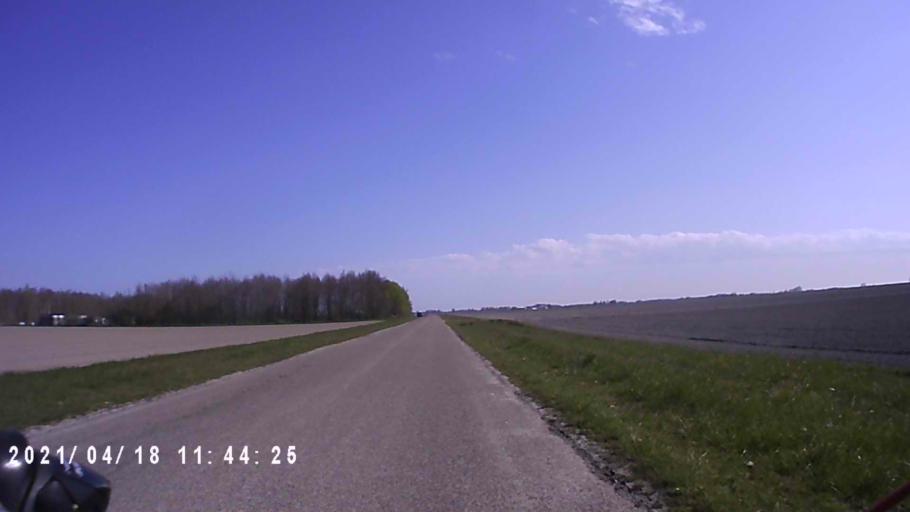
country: NL
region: Groningen
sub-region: Gemeente Zuidhorn
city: Grijpskerk
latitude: 53.3201
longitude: 6.2572
